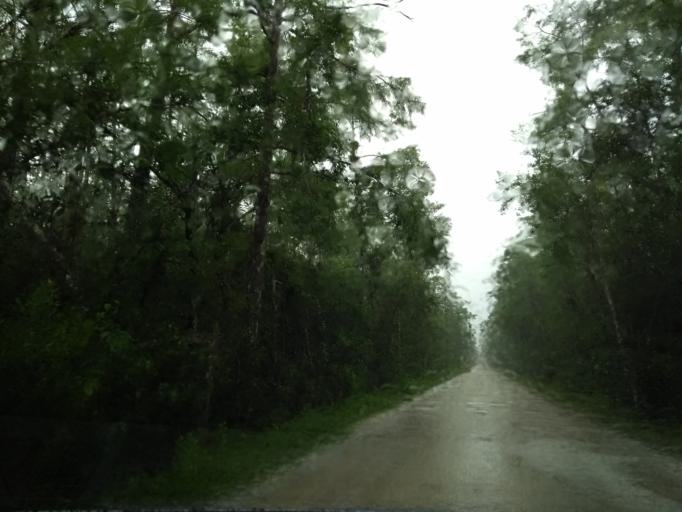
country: US
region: Florida
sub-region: Miami-Dade County
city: The Hammocks
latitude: 25.7824
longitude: -81.0932
